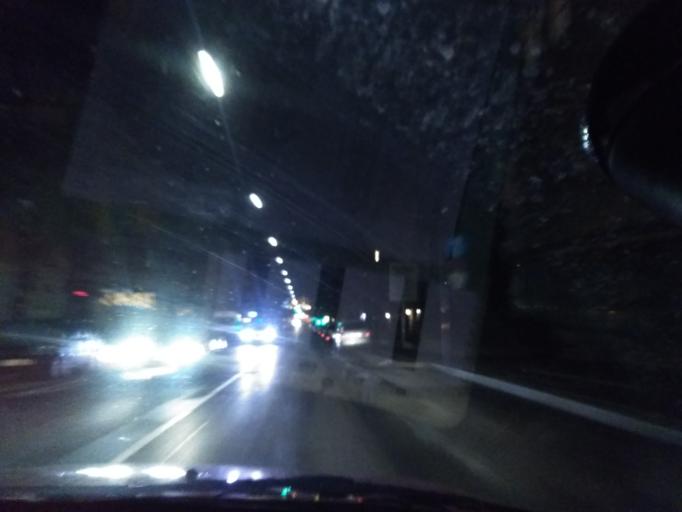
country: AT
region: Vienna
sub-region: Wien Stadt
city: Vienna
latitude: 48.1955
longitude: 16.3180
